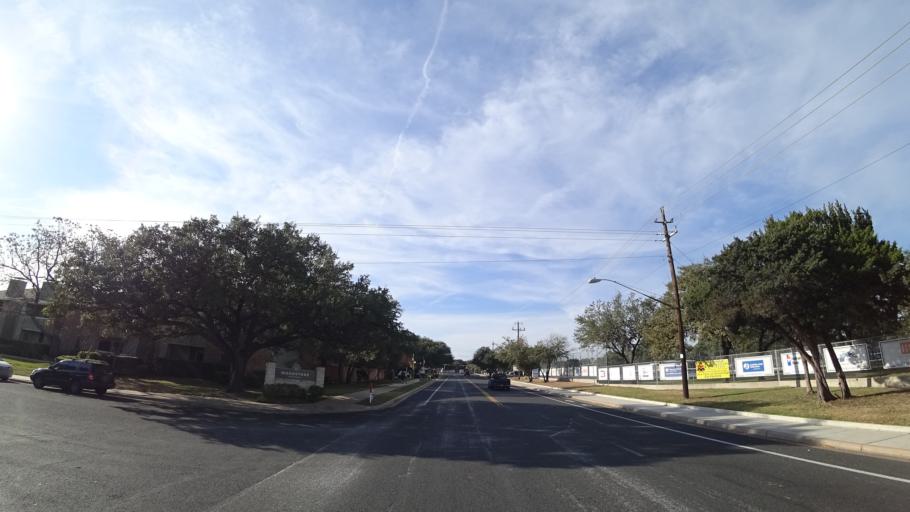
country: US
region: Texas
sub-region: Williamson County
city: Jollyville
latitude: 30.3732
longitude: -97.7532
